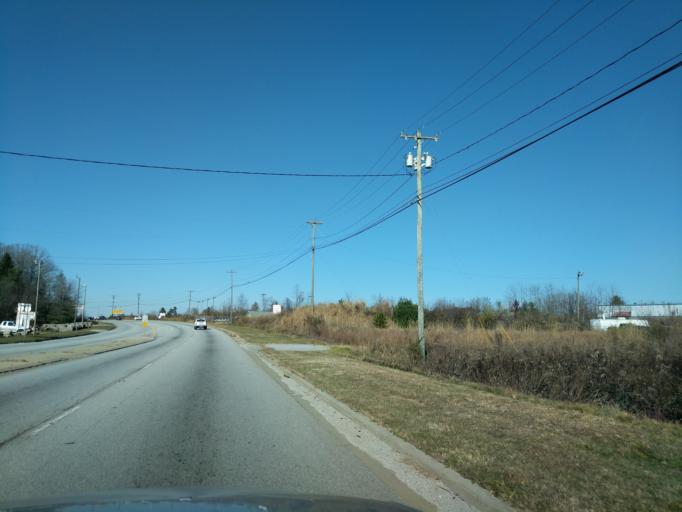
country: US
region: North Carolina
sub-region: Henderson County
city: Fletcher
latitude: 35.4016
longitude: -82.5091
